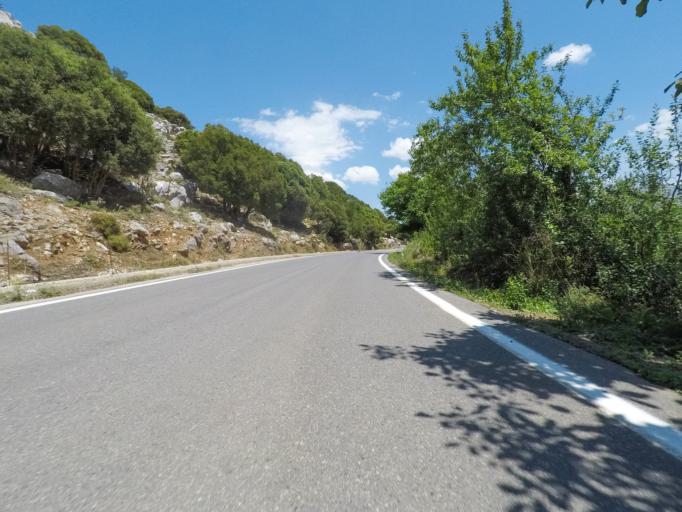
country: GR
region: Crete
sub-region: Nomos Irakleiou
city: Mokhos
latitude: 35.1967
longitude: 25.4545
